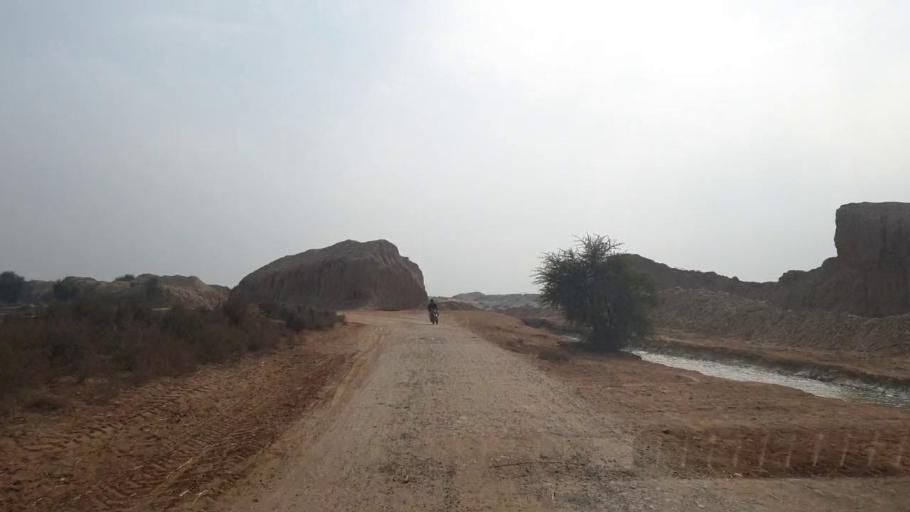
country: PK
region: Sindh
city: Sann
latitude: 26.0166
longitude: 68.1445
